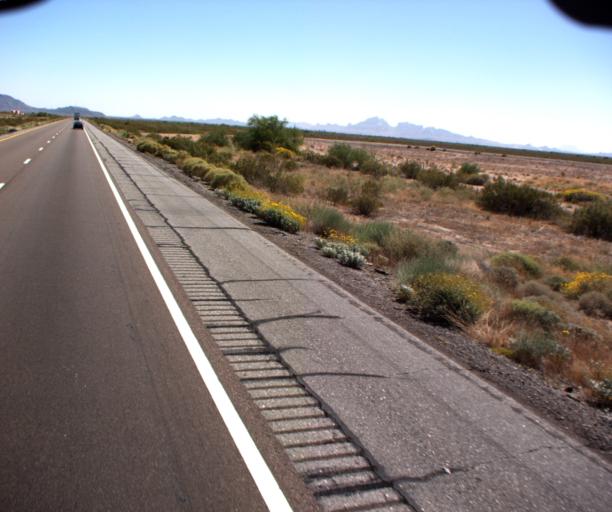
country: US
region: Arizona
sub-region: La Paz County
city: Salome
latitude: 33.5466
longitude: -113.2074
